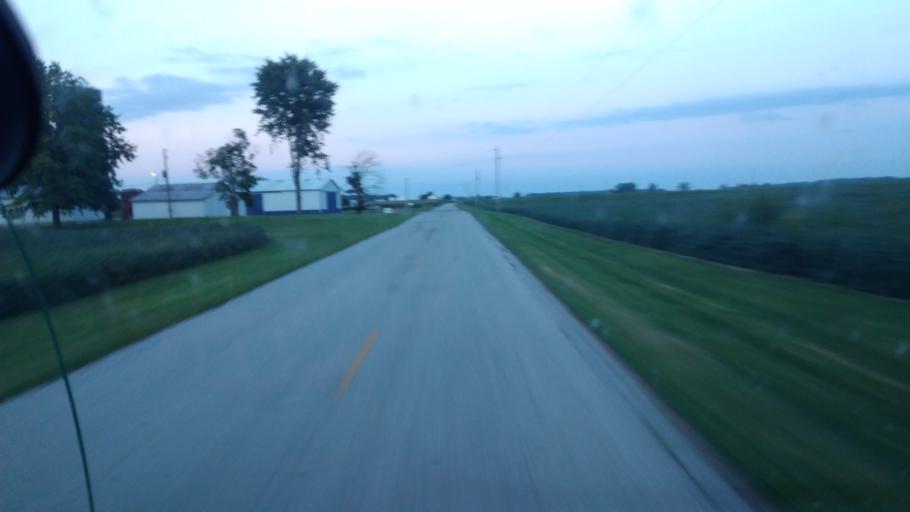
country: US
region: Ohio
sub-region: Hardin County
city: Forest
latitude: 40.6723
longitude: -83.4732
